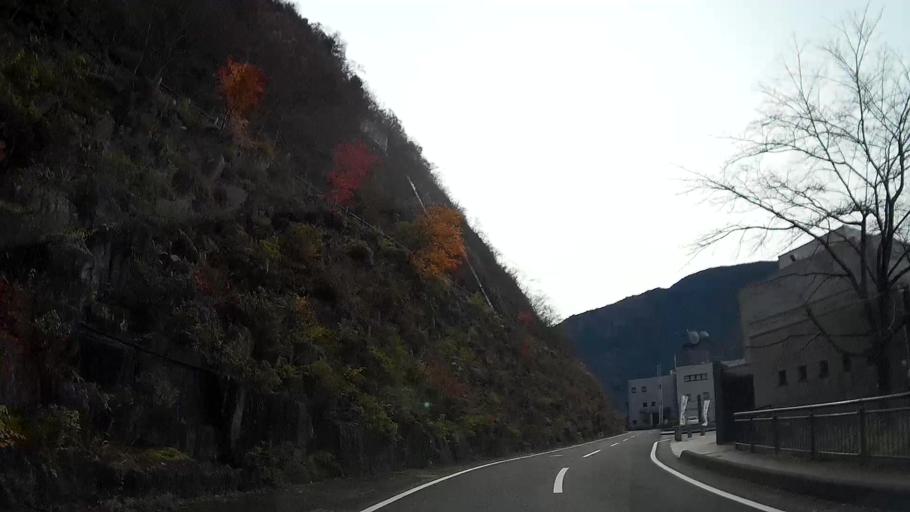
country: JP
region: Saitama
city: Chichibu
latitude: 35.9534
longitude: 139.0547
